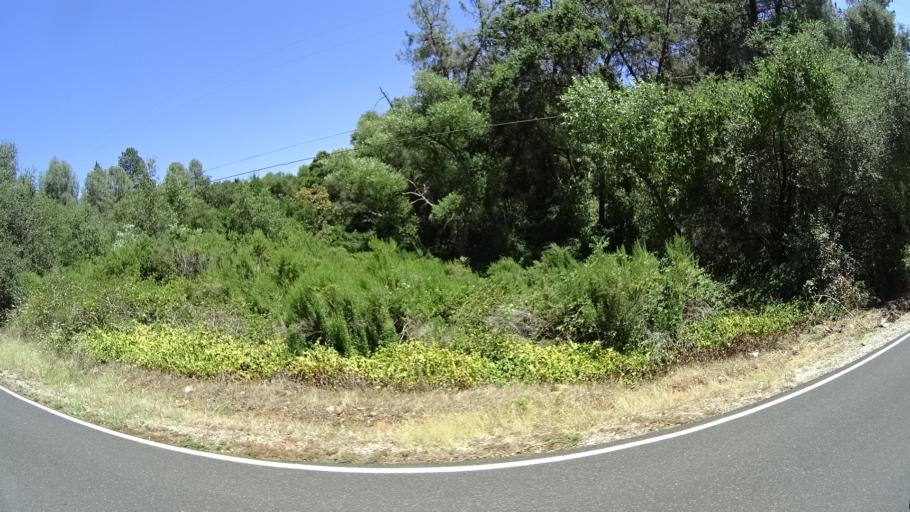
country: US
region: California
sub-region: Calaveras County
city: Angels Camp
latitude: 38.1117
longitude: -120.5213
